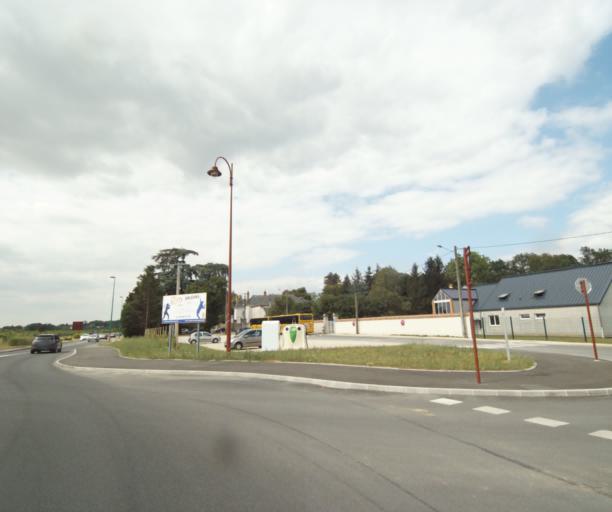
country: FR
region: Centre
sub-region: Departement du Loiret
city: Saint-Pryve-Saint-Mesmin
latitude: 47.8836
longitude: 1.8644
